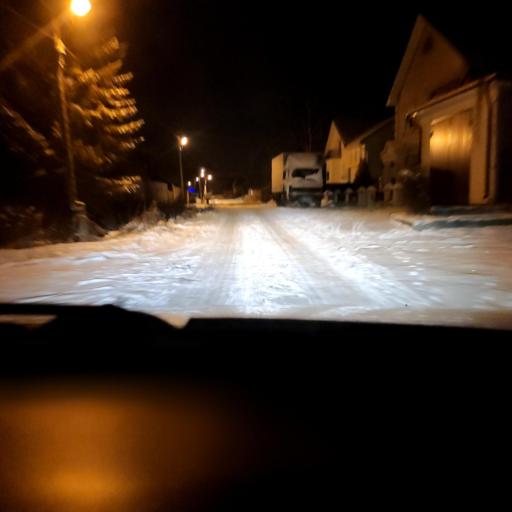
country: RU
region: Perm
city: Kondratovo
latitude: 58.0491
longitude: 56.0451
